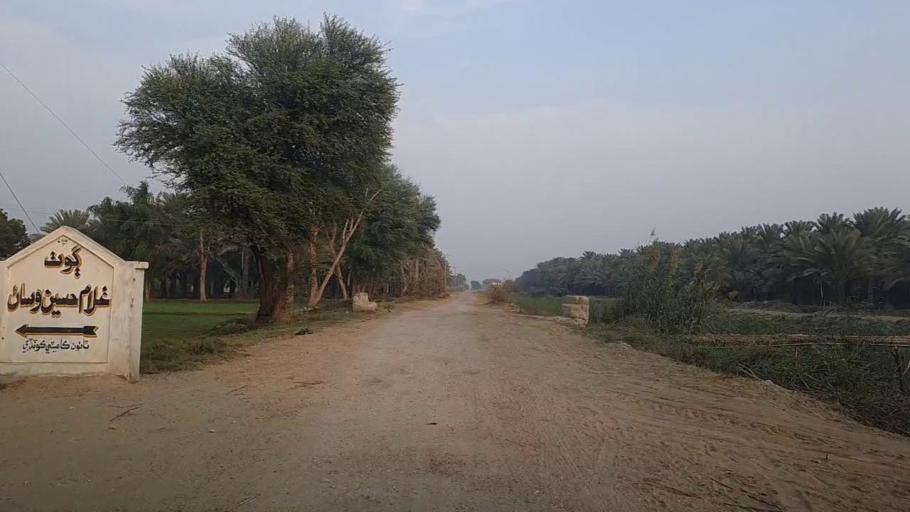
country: PK
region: Sindh
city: Kot Diji
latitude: 27.3581
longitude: 68.6526
